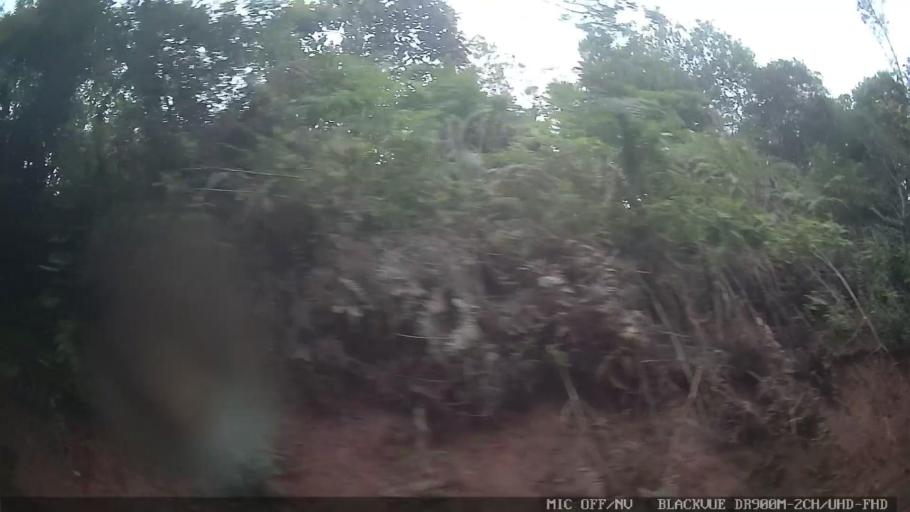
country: BR
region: Sao Paulo
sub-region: Suzano
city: Suzano
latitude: -23.6827
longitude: -46.2371
